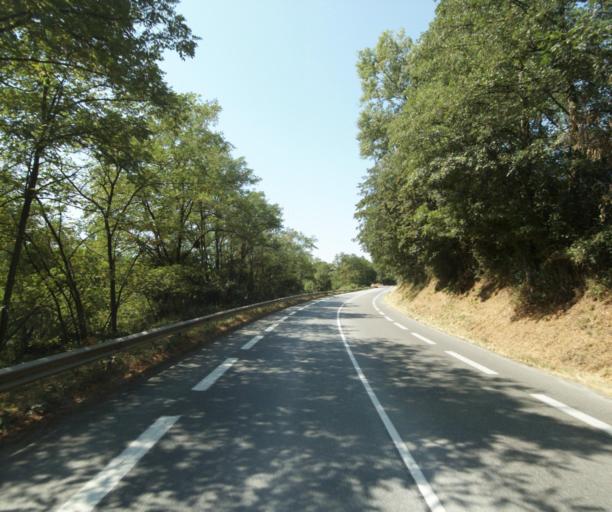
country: FR
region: Rhone-Alpes
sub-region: Departement du Rhone
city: Bessenay
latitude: 45.7857
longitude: 4.5811
